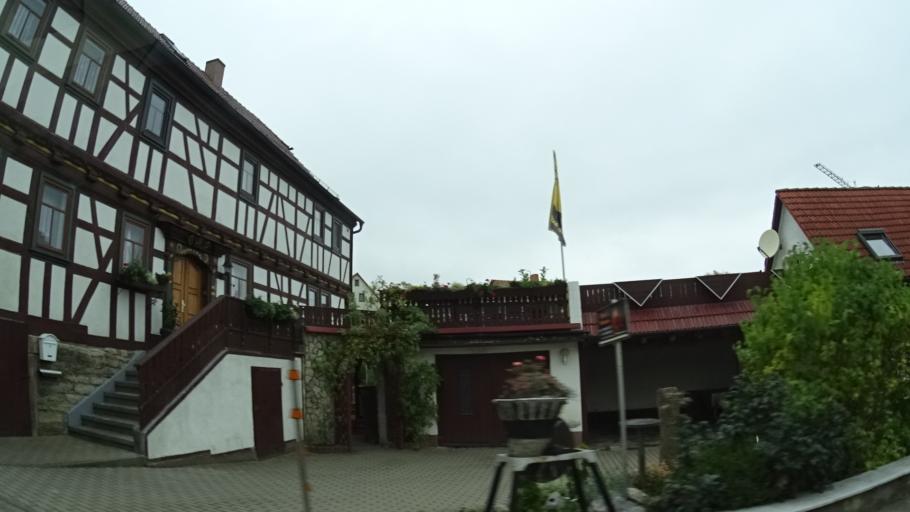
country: DE
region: Thuringia
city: Kaltensundheim
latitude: 50.6062
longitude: 10.1585
